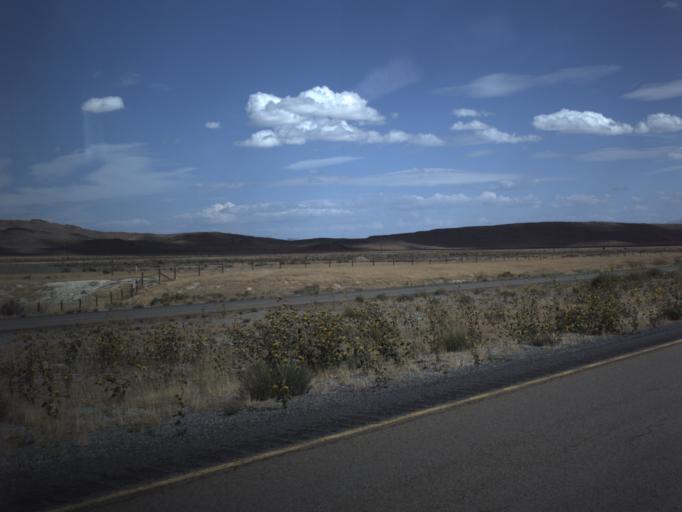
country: US
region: Utah
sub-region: Tooele County
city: Grantsville
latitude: 40.7899
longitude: -112.8312
